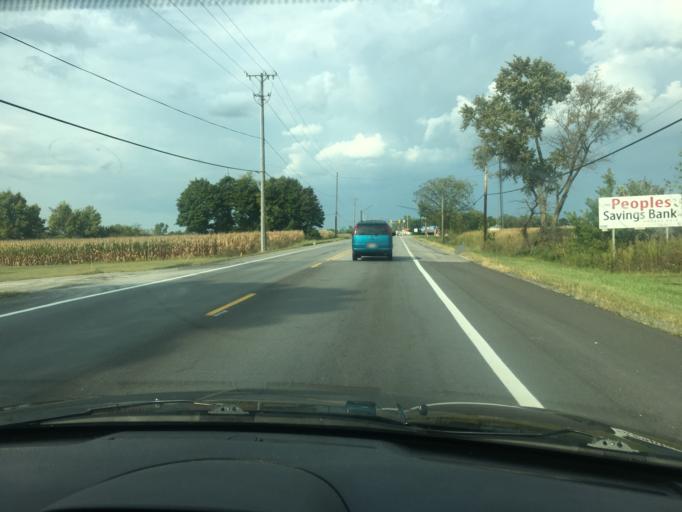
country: US
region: Ohio
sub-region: Champaign County
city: Urbana
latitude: 40.0858
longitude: -83.7591
